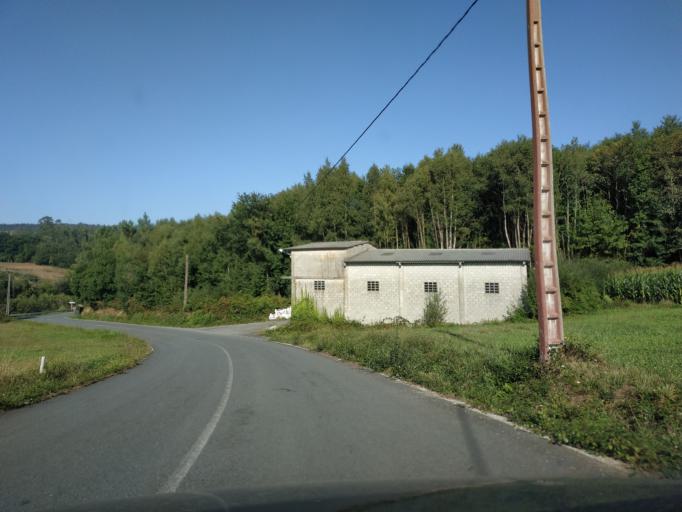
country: ES
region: Galicia
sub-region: Provincia da Coruna
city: Cerceda
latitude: 43.2315
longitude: -8.4894
